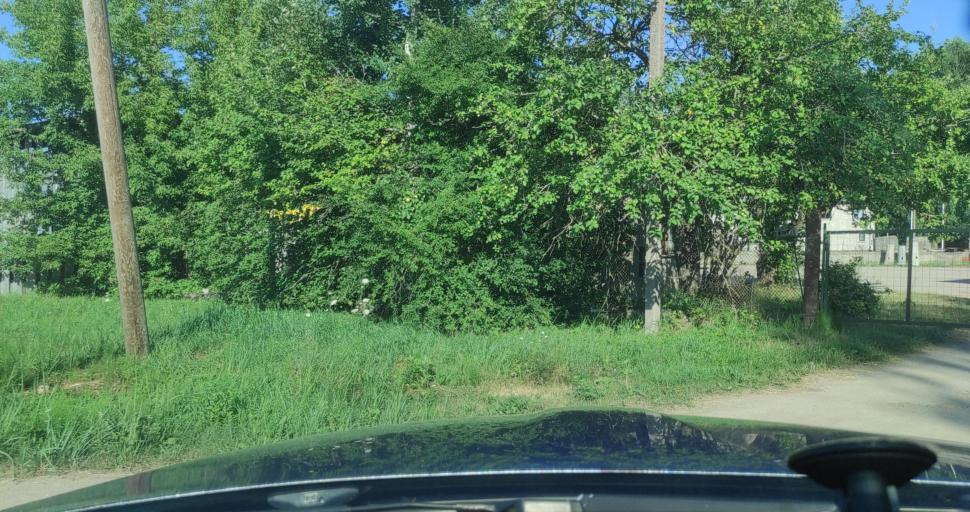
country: LV
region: Skrunda
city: Skrunda
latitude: 56.6829
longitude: 22.0045
